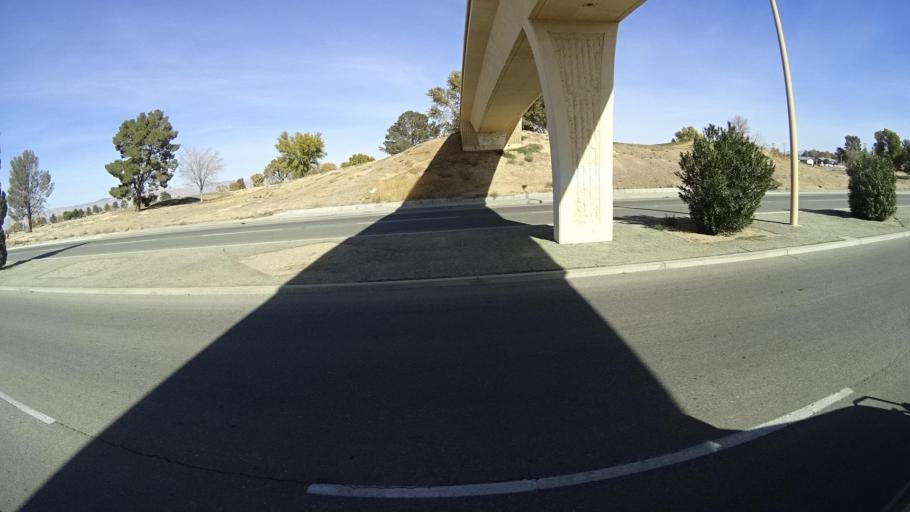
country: US
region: California
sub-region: Kern County
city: California City
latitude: 35.1259
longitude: -117.9529
